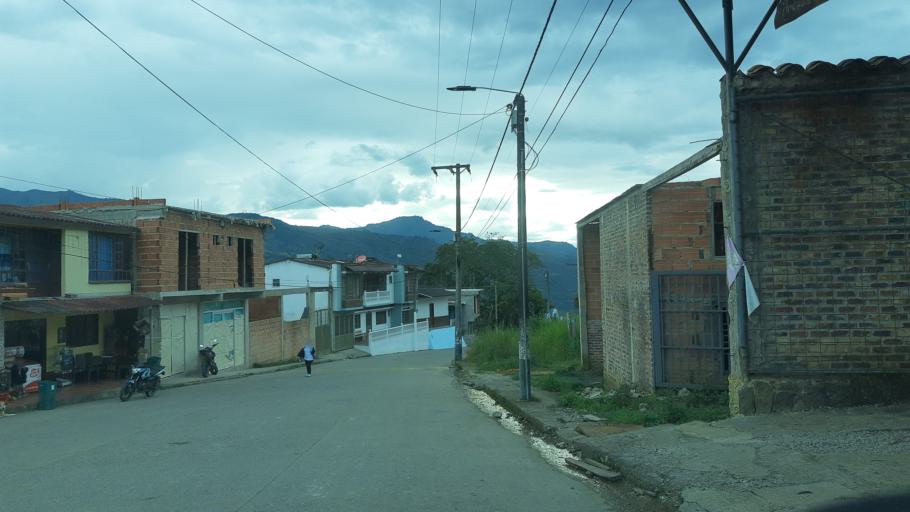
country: CO
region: Boyaca
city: Chivor
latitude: 4.9730
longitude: -73.3208
